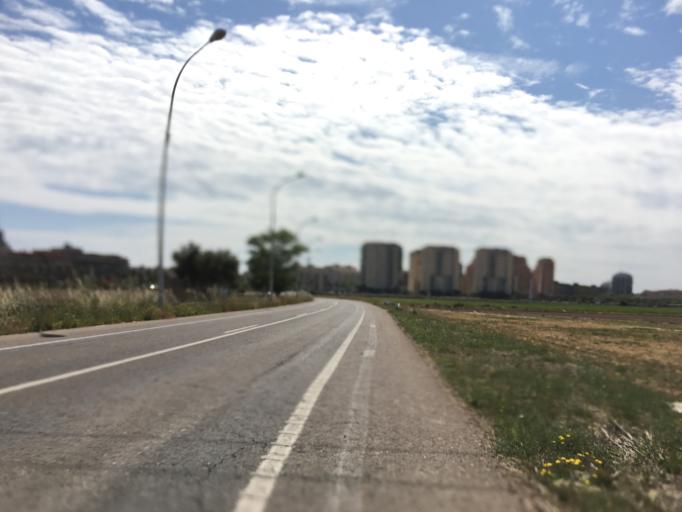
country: ES
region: Valencia
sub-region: Provincia de Valencia
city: Mislata
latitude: 39.4888
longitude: -0.4104
